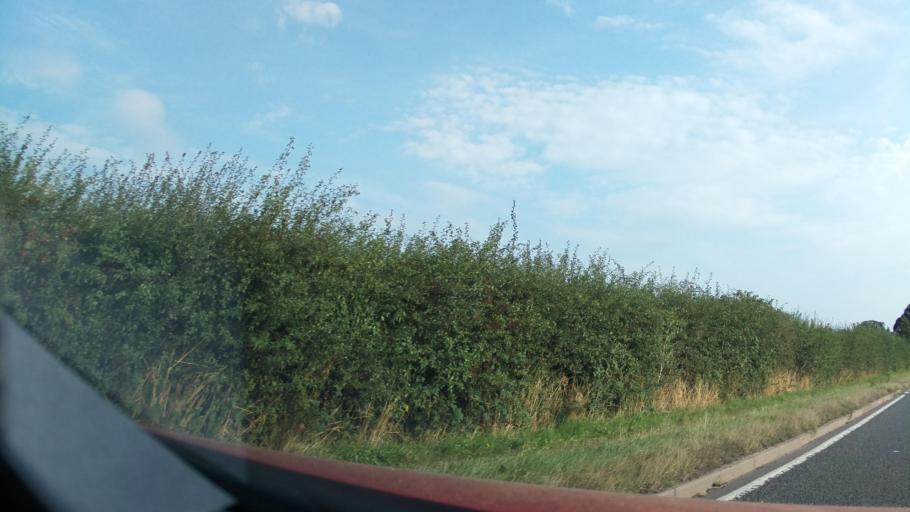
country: GB
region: England
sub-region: Warwickshire
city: Studley
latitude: 52.2507
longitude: -1.8871
